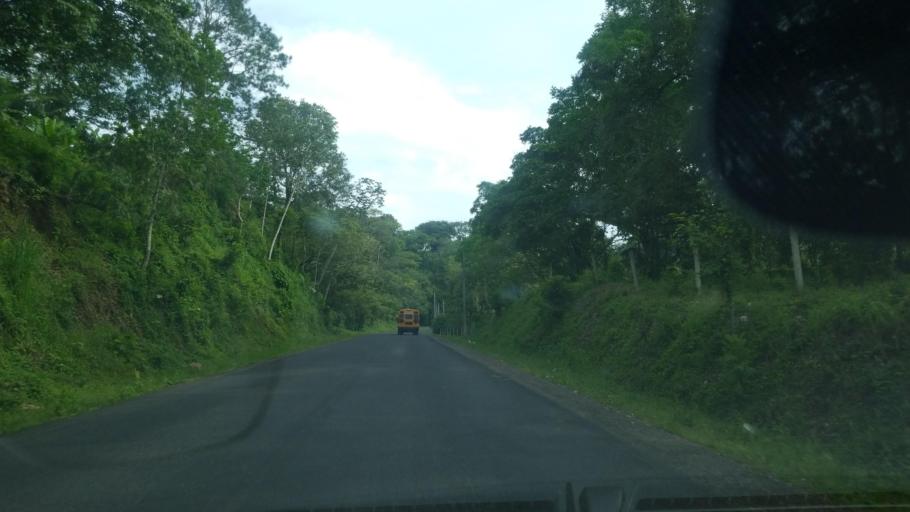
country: HN
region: Santa Barbara
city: Petoa
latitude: 15.2207
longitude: -88.2678
